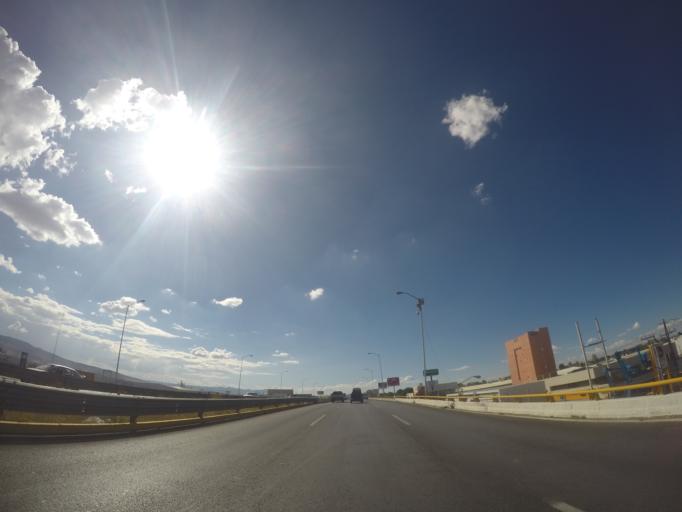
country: MX
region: San Luis Potosi
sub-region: Soledad de Graciano Sanchez
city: Soledad de Graciano Sanchez
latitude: 22.1166
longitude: -100.9049
